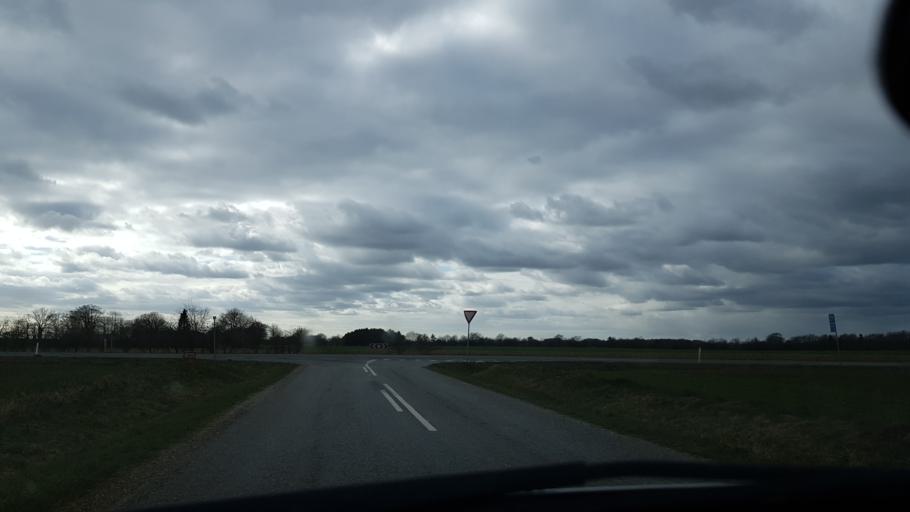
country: DK
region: South Denmark
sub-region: Vejen Kommune
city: Holsted
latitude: 55.4041
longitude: 8.8846
